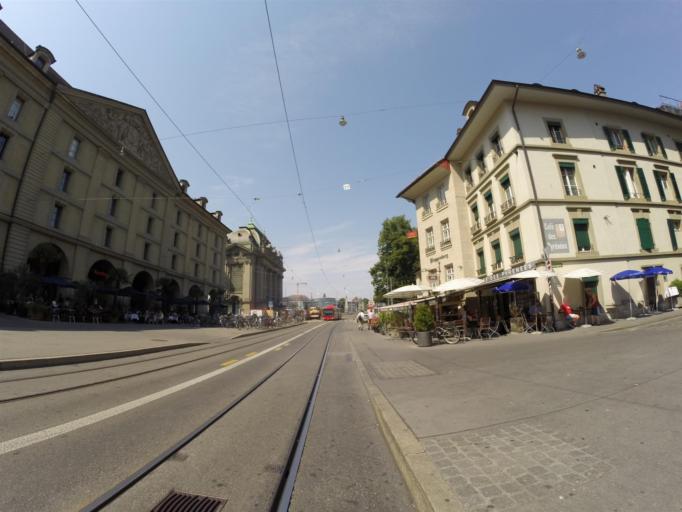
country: CH
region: Bern
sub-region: Bern-Mittelland District
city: Bern
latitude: 46.9485
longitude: 7.4477
